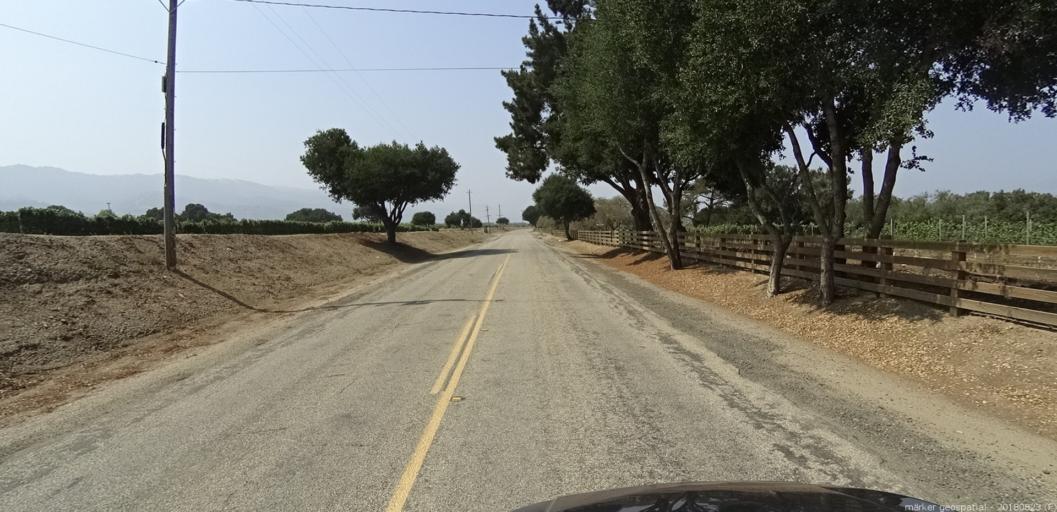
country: US
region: California
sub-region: Monterey County
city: Gonzales
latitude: 36.4545
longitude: -121.4433
